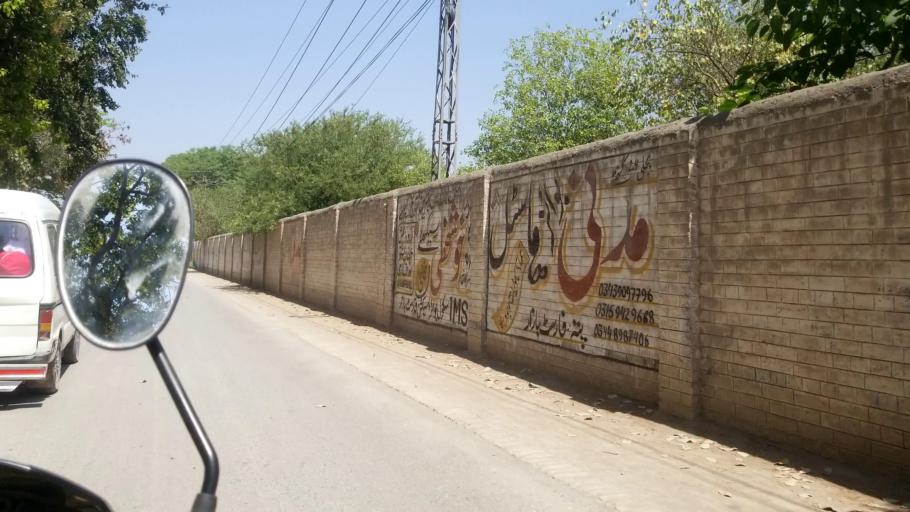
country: PK
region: Khyber Pakhtunkhwa
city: Peshawar
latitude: 34.0207
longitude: 71.4844
